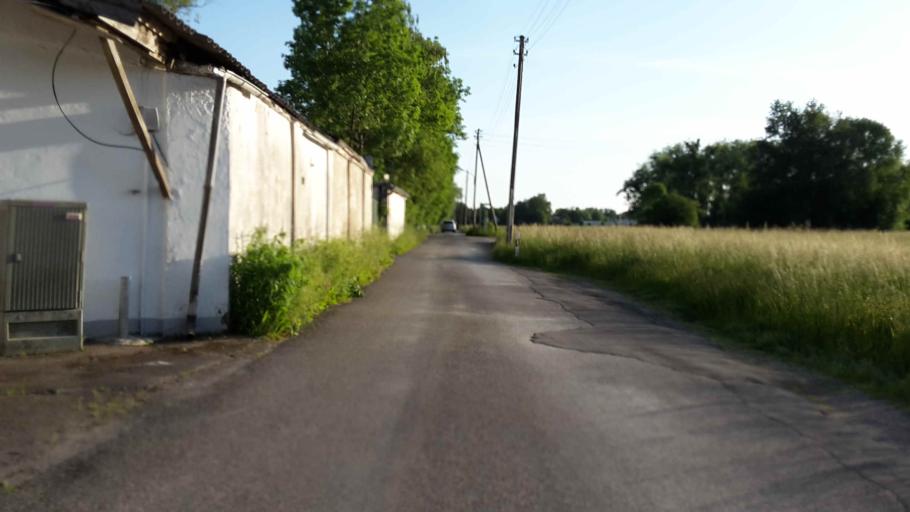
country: DE
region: Bavaria
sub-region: Upper Bavaria
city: Karlsfeld
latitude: 48.2059
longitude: 11.5055
